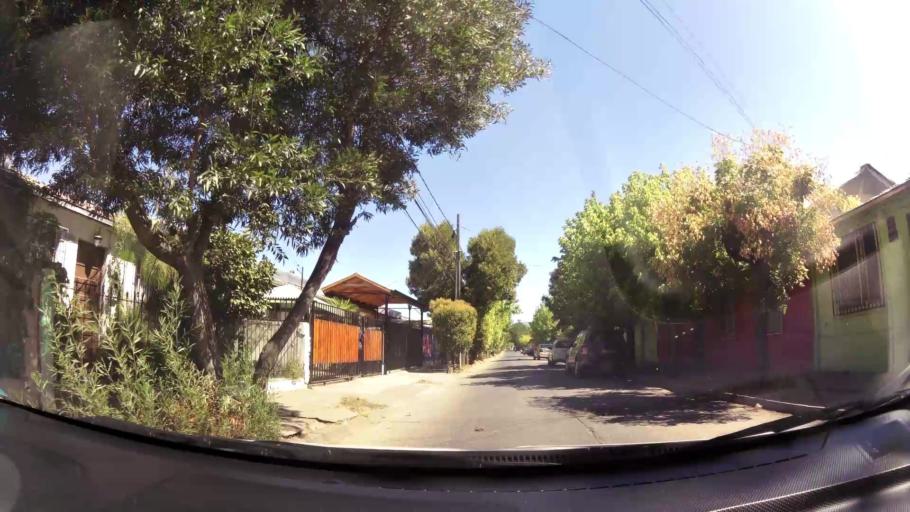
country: CL
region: O'Higgins
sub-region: Provincia de Colchagua
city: Chimbarongo
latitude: -34.5790
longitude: -70.9912
